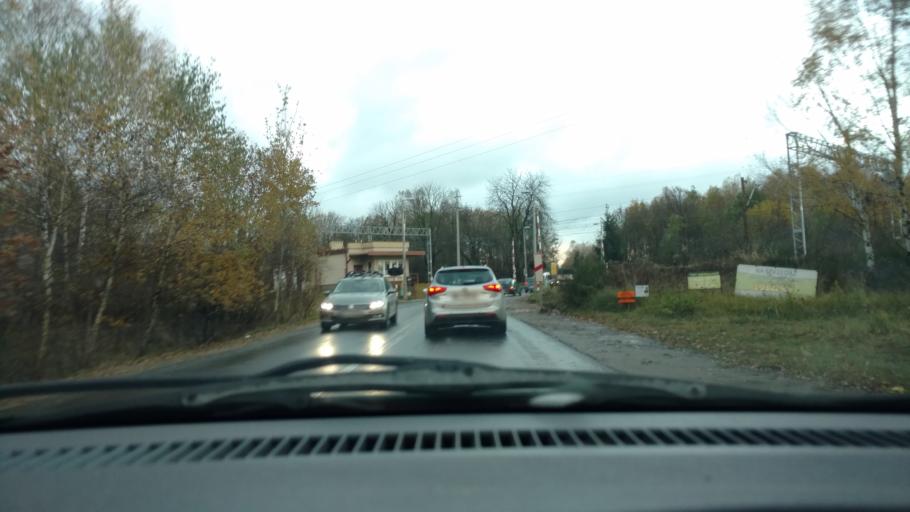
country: PL
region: Lodz Voivodeship
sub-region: Powiat lodzki wschodni
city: Andrespol
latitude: 51.7566
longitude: 19.5777
